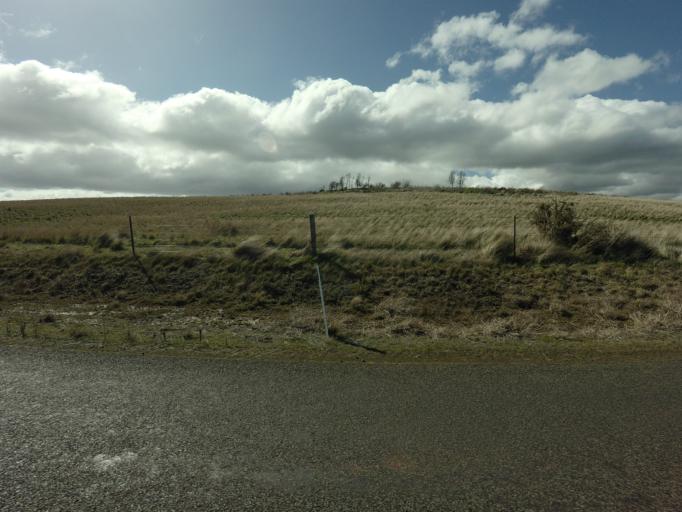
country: AU
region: Tasmania
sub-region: Northern Midlands
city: Evandale
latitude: -41.9162
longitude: 147.4728
